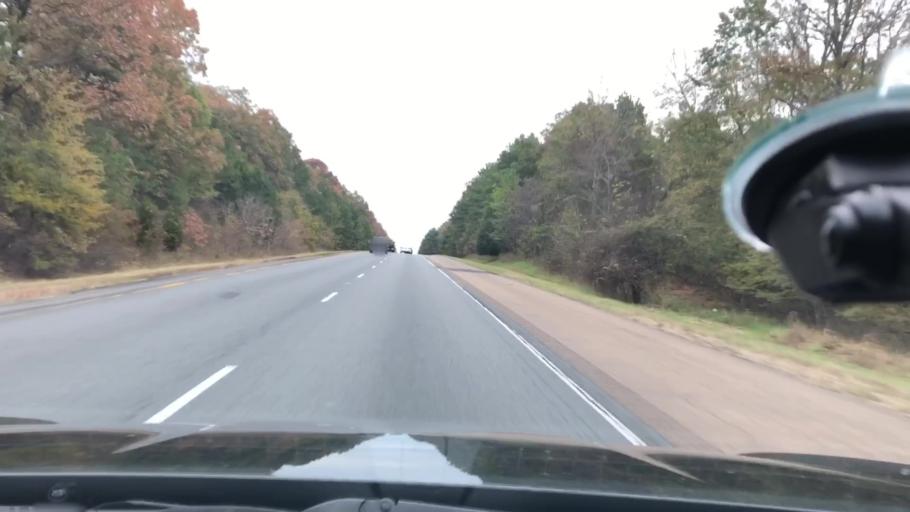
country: US
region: Arkansas
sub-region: Clark County
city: Gurdon
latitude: 33.9367
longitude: -93.2503
